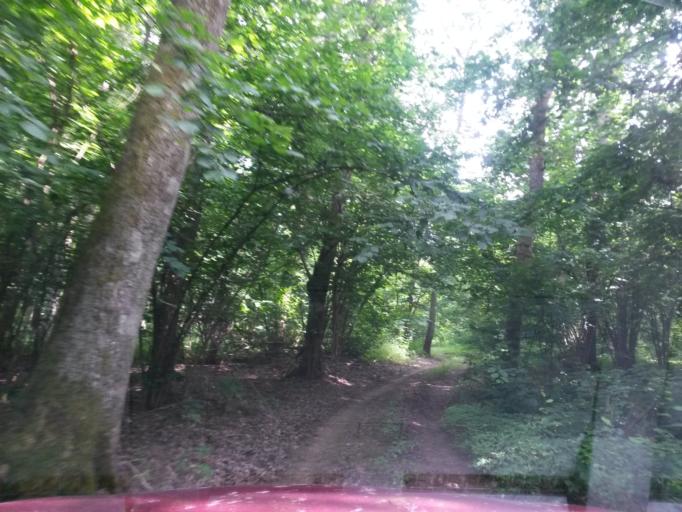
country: SK
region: Kosicky
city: Moldava nad Bodvou
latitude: 48.6433
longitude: 21.1011
